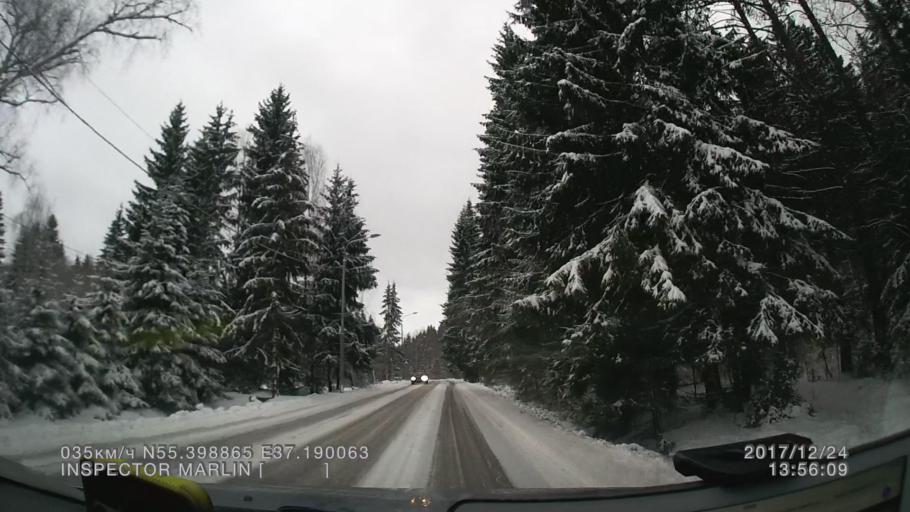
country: RU
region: Moskovskaya
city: Troitsk
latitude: 55.3988
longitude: 37.1902
